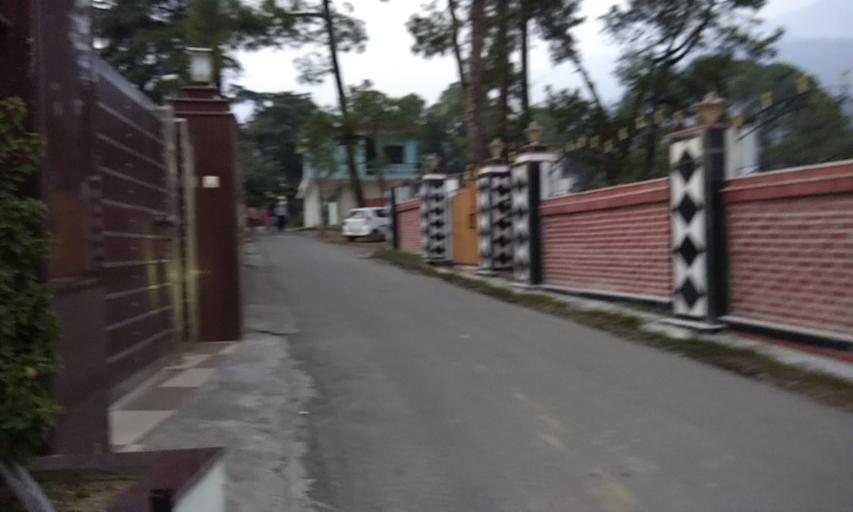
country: IN
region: Himachal Pradesh
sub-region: Kangra
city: Palampur
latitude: 32.1170
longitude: 76.5421
